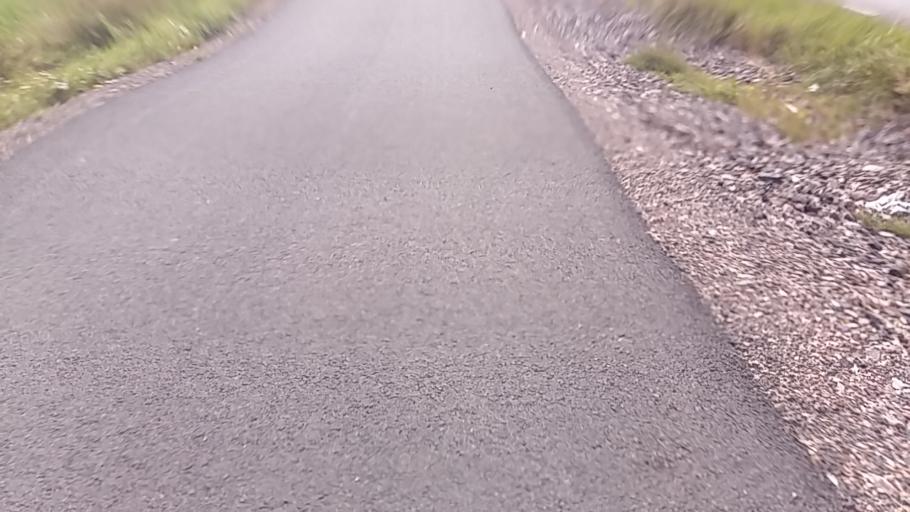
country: SE
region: Joenkoeping
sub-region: Jonkopings Kommun
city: Odensjo
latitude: 57.7298
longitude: 14.1448
